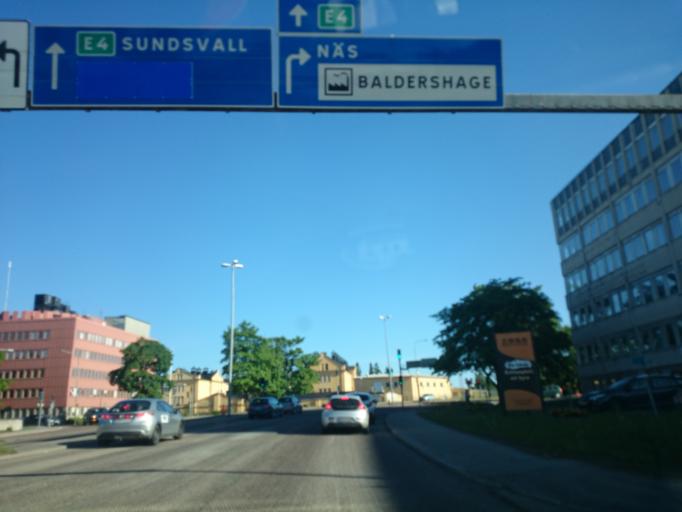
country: SE
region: Vaesternorrland
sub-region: Haernoesands Kommun
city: Haernoesand
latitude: 62.6298
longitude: 17.9313
